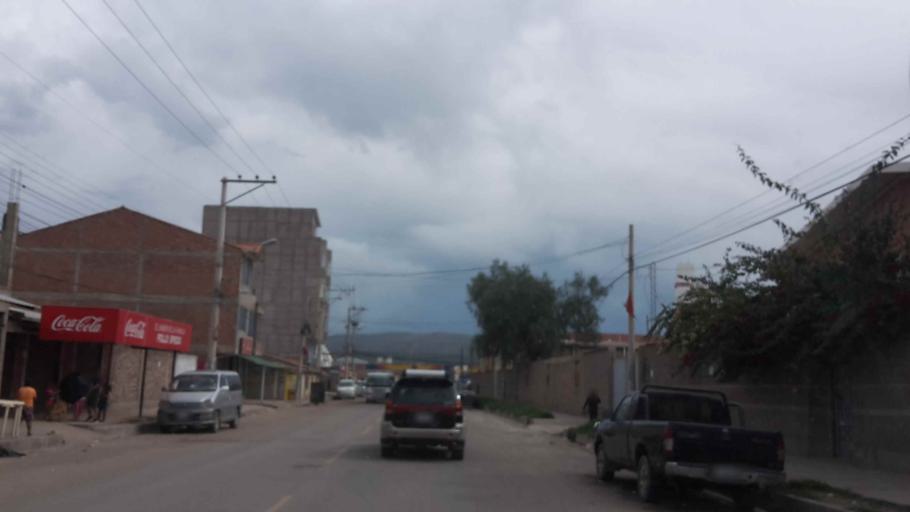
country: BO
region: Cochabamba
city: Cochabamba
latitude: -17.3898
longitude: -66.2507
